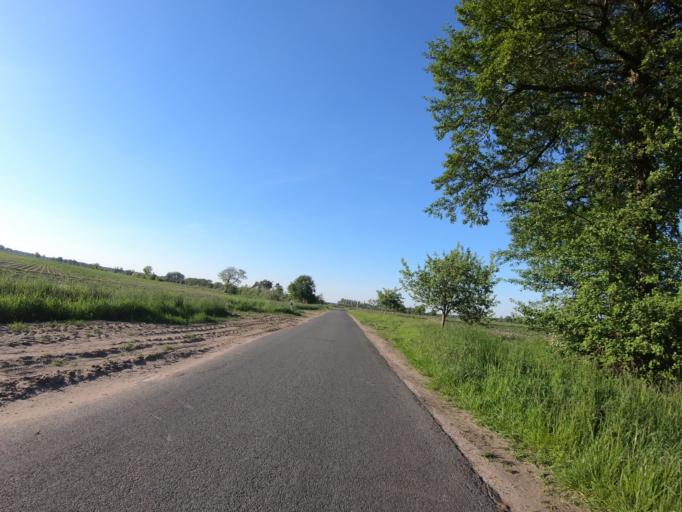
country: DE
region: Lower Saxony
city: Wagenhoff
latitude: 52.5285
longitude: 10.5594
